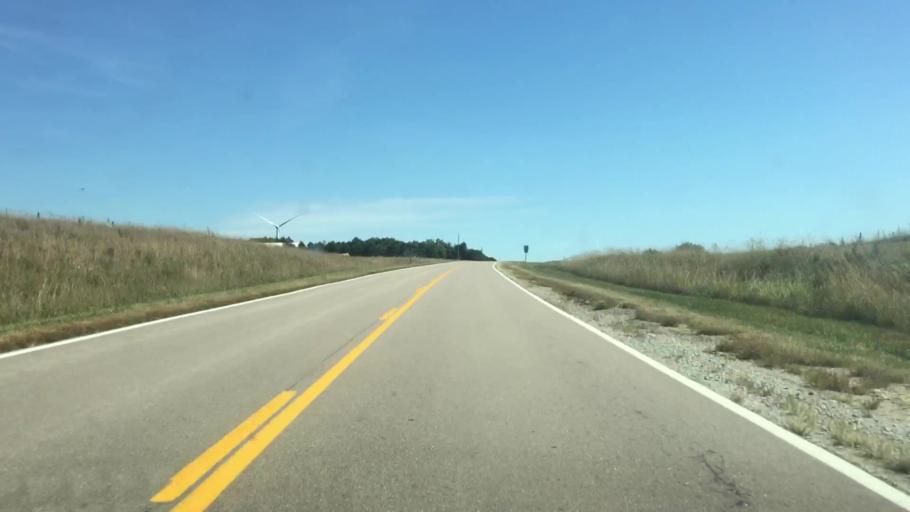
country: US
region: Kansas
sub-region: Washington County
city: Washington
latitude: 40.0453
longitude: -96.9463
